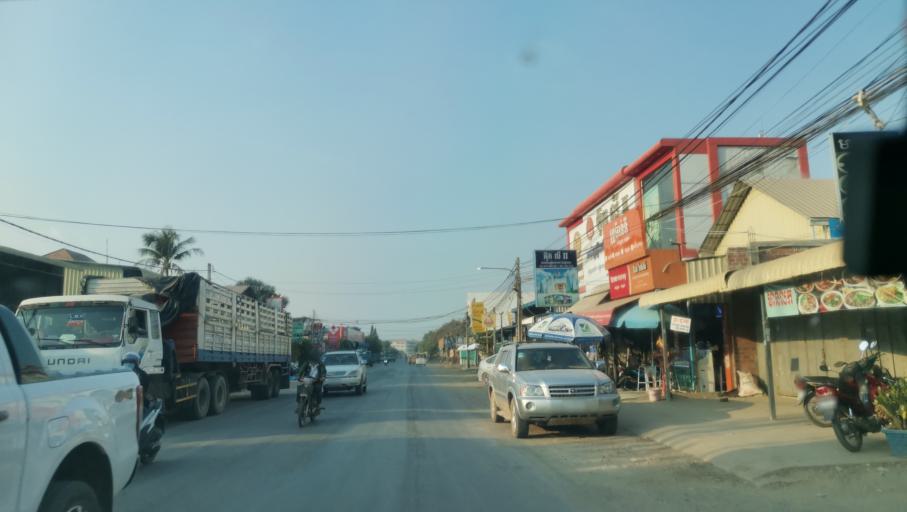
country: KH
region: Battambang
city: Battambang
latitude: 13.0893
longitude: 103.1917
